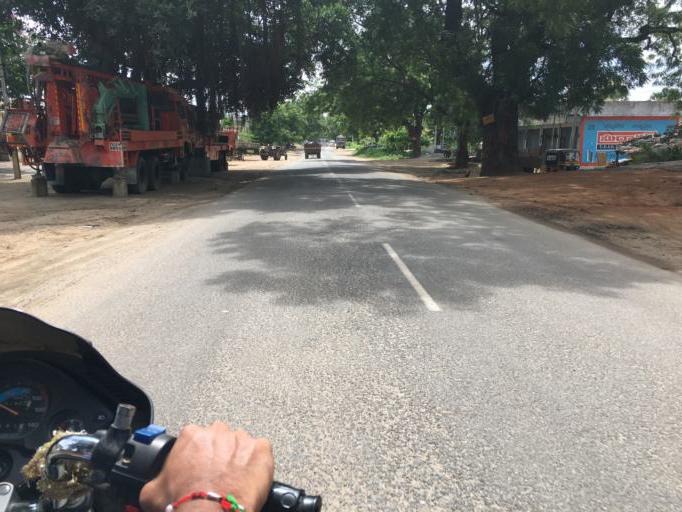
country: IN
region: Telangana
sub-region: Nalgonda
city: Nalgonda
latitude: 17.1671
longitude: 79.4151
